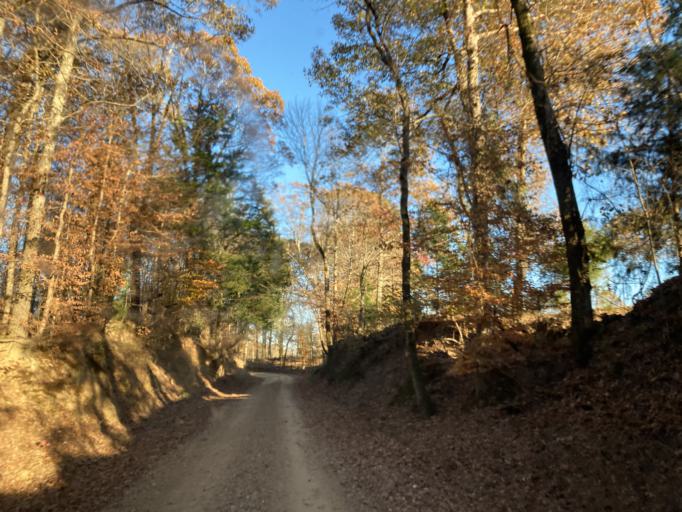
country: US
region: Mississippi
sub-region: Yazoo County
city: Yazoo City
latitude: 32.9461
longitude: -90.2840
